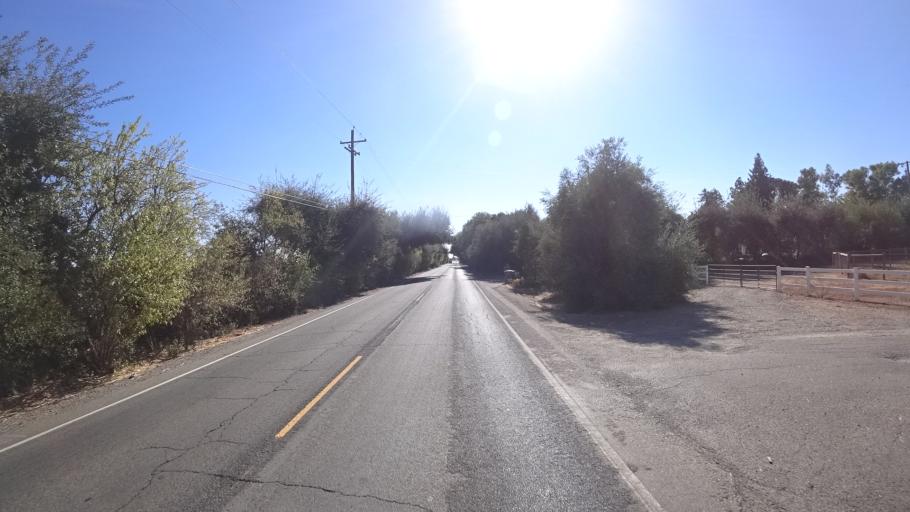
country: US
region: California
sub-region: Yolo County
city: Davis
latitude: 38.5509
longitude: -121.8033
